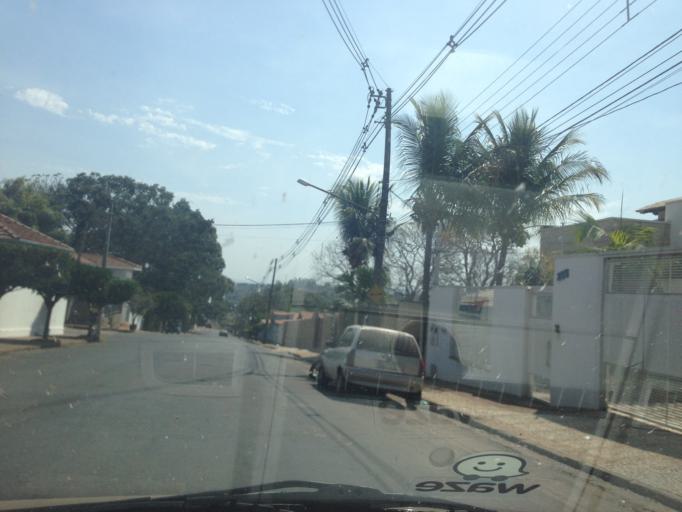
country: BR
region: Sao Paulo
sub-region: Casa Branca
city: Casa Branca
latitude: -21.7763
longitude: -47.0770
